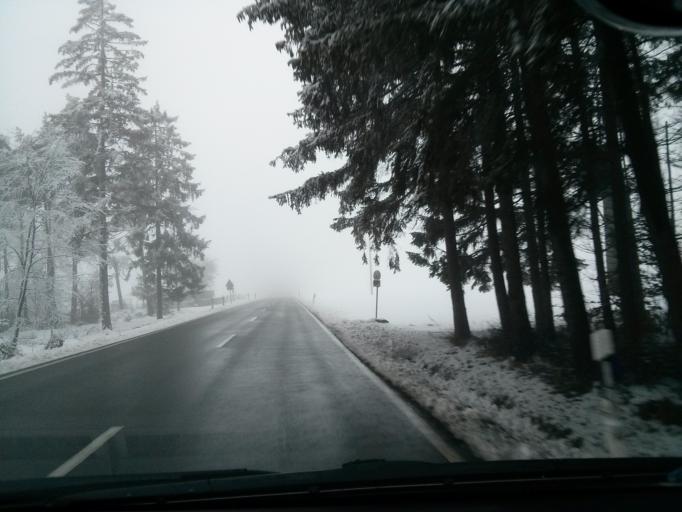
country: DE
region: Rheinland-Pfalz
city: Hummel
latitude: 50.5208
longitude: 6.8265
